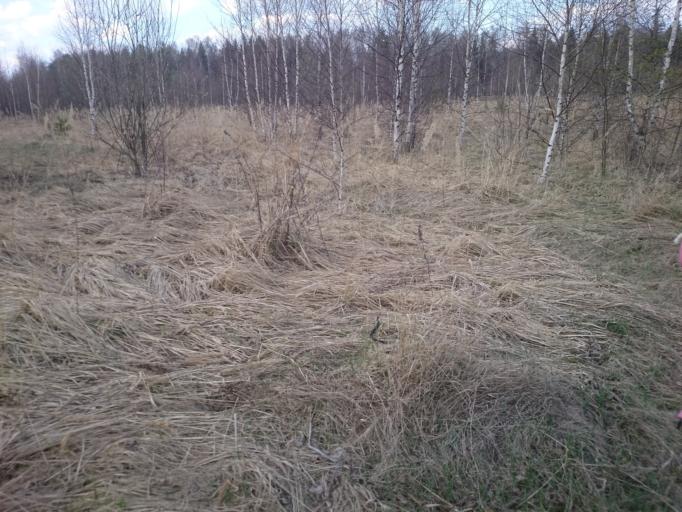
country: RU
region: Moskovskaya
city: Klin
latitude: 56.4018
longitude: 36.6806
